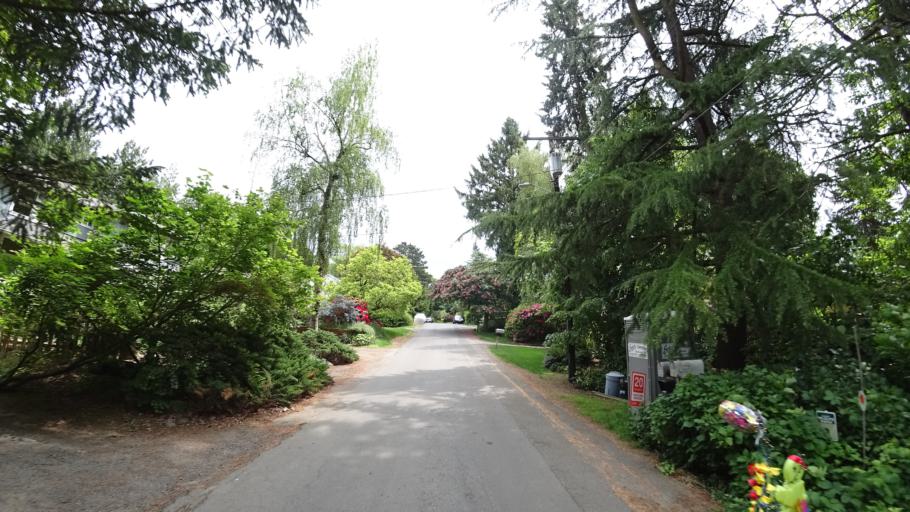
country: US
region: Oregon
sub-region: Washington County
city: Garden Home-Whitford
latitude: 45.4731
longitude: -122.7351
